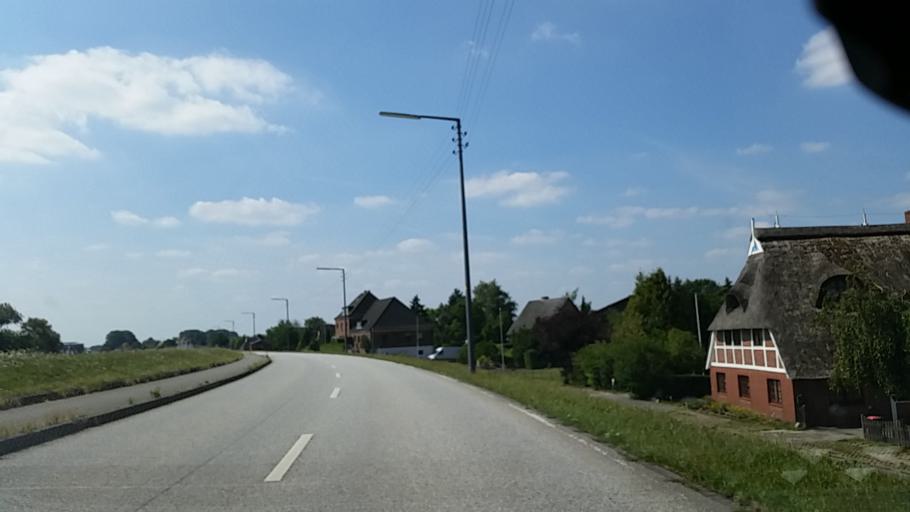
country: DE
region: Lower Saxony
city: Winsen
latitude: 53.4036
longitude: 10.1946
